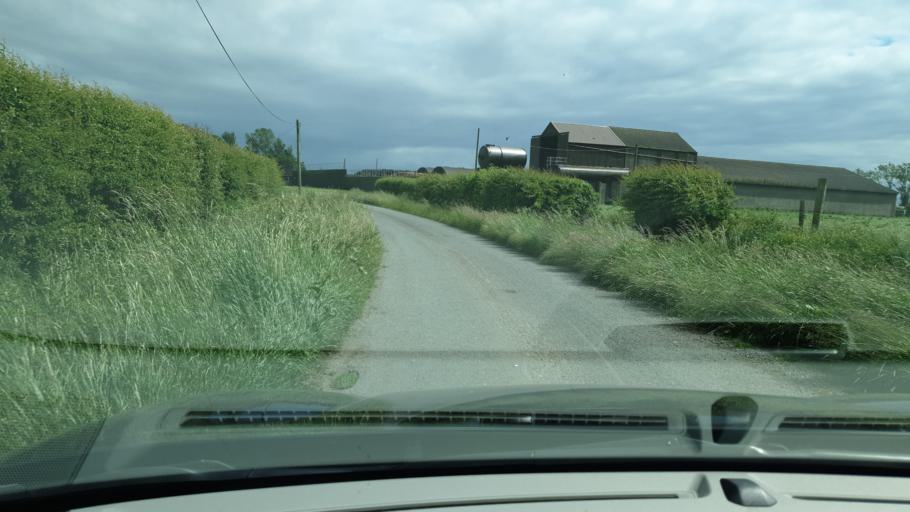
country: IE
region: Leinster
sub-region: An Mhi
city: Ratoath
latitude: 53.4545
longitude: -6.4539
